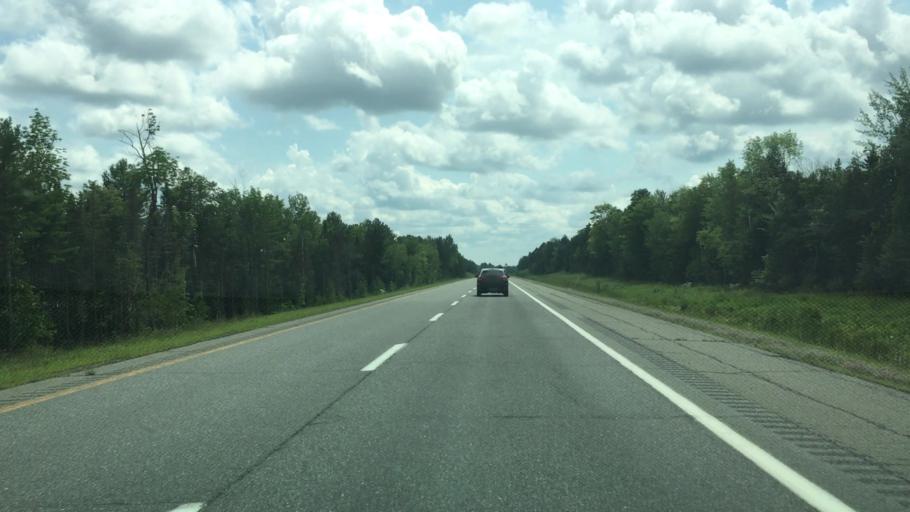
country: US
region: Maine
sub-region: Penobscot County
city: Howland
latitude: 45.3032
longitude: -68.6618
